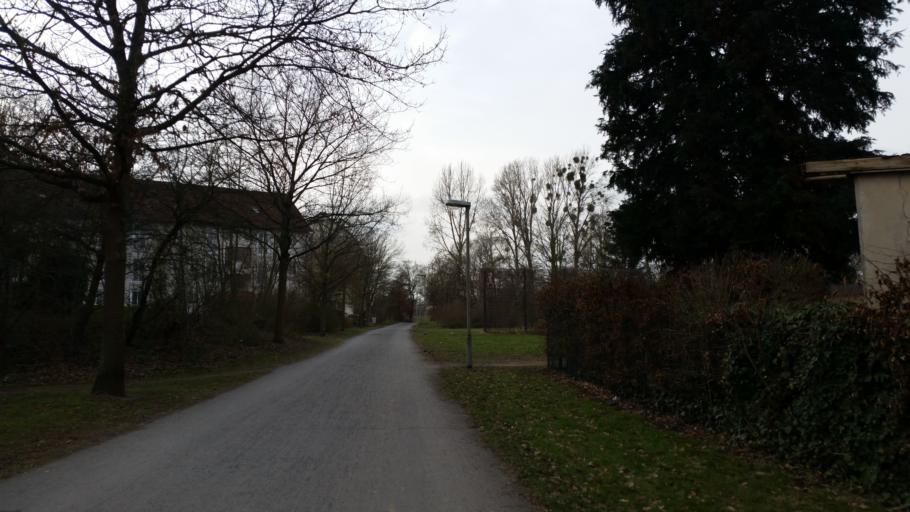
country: DE
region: Lower Saxony
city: Hannover
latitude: 52.4008
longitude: 9.7208
